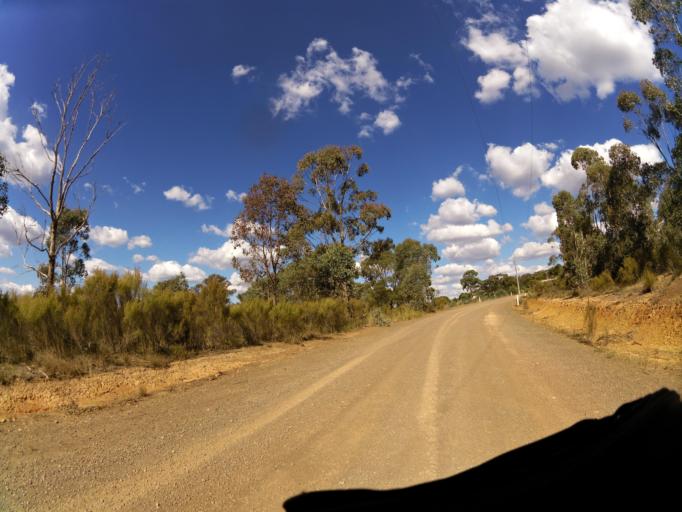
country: AU
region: Victoria
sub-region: Greater Bendigo
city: Kennington
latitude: -36.9538
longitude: 144.7764
